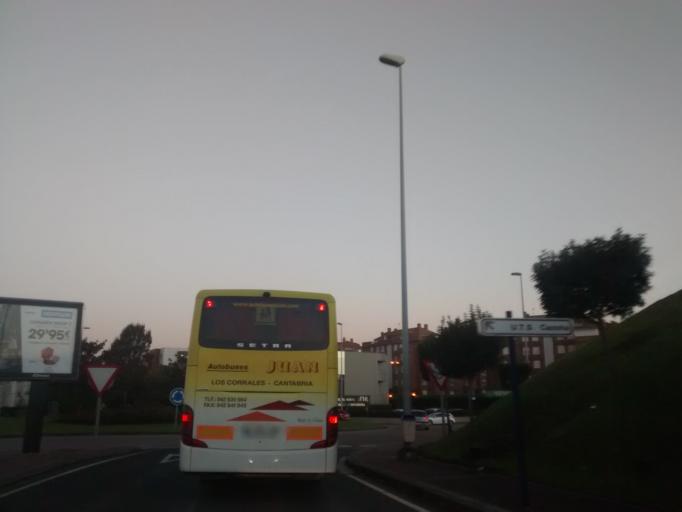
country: ES
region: Cantabria
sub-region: Provincia de Cantabria
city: Santa Cruz de Bezana
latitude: 43.4574
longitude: -3.8595
